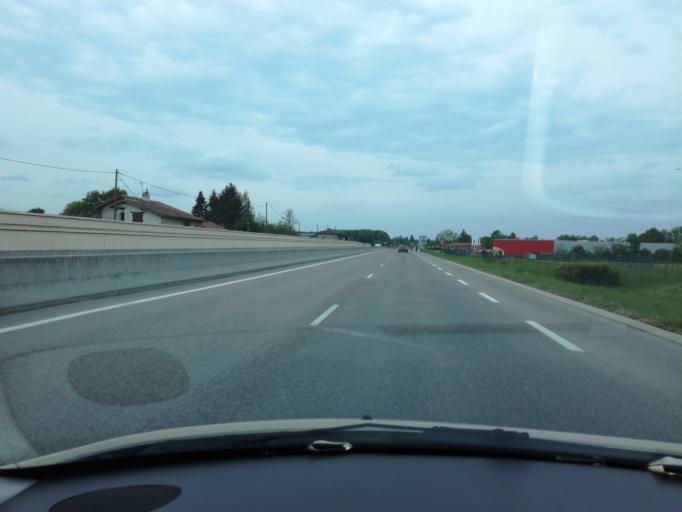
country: FR
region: Rhone-Alpes
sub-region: Departement de l'Ain
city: Montagnat
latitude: 46.1528
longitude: 5.2765
